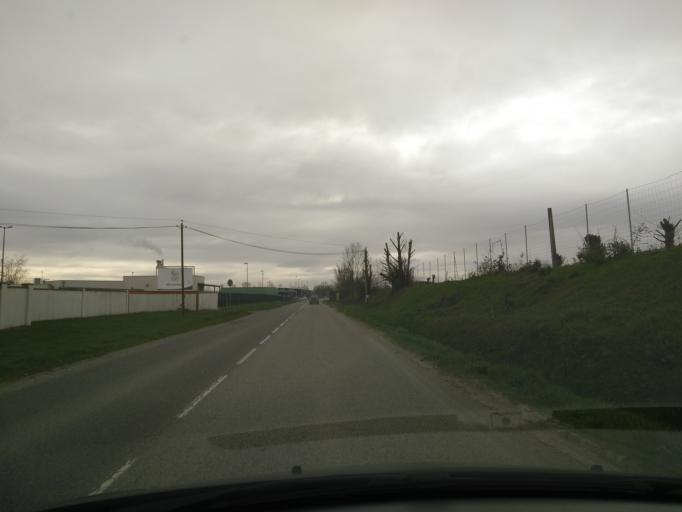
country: FR
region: Midi-Pyrenees
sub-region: Departement de la Haute-Garonne
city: Cugnaux
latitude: 43.5323
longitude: 1.3668
